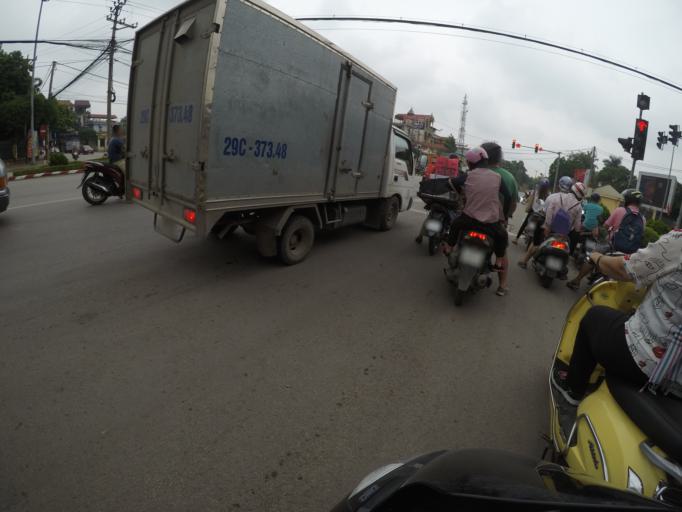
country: VN
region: Ha Noi
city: Soc Son
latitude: 21.2570
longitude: 105.8481
